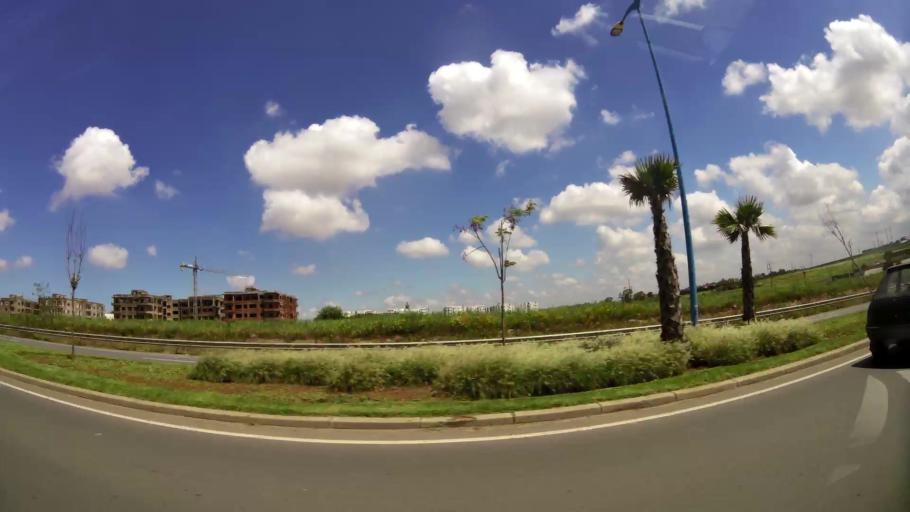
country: MA
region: Grand Casablanca
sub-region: Casablanca
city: Casablanca
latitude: 33.5182
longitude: -7.6152
